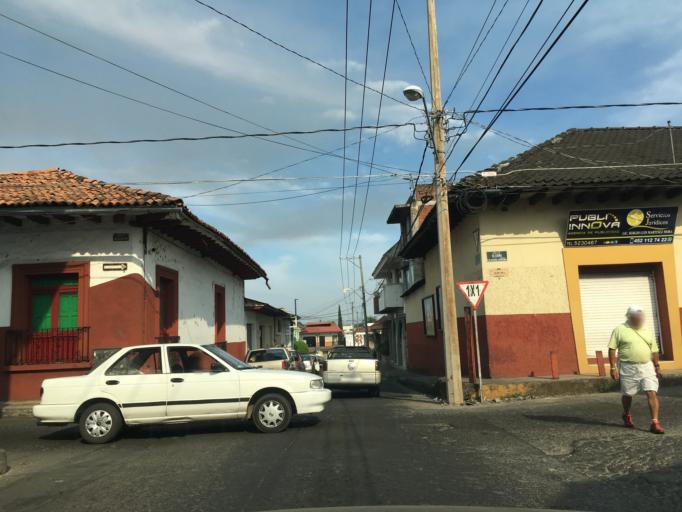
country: MX
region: Michoacan
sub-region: Uruapan
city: Uruapan
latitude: 19.4181
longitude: -102.0614
